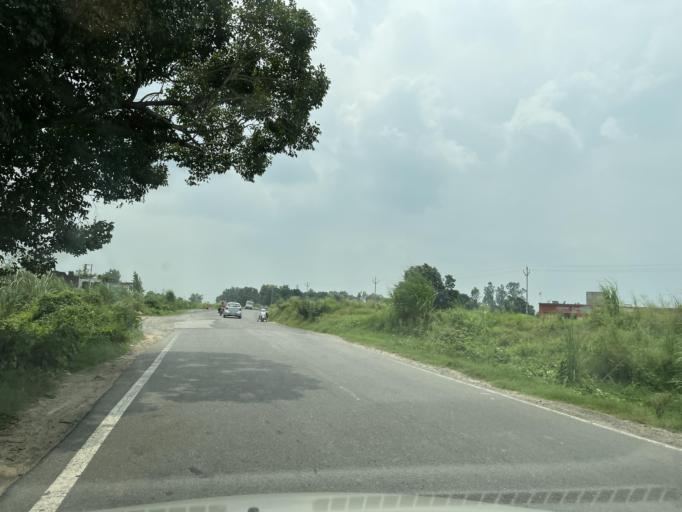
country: IN
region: Uttar Pradesh
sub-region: Bijnor
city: Najibabad
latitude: 29.5759
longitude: 78.3386
